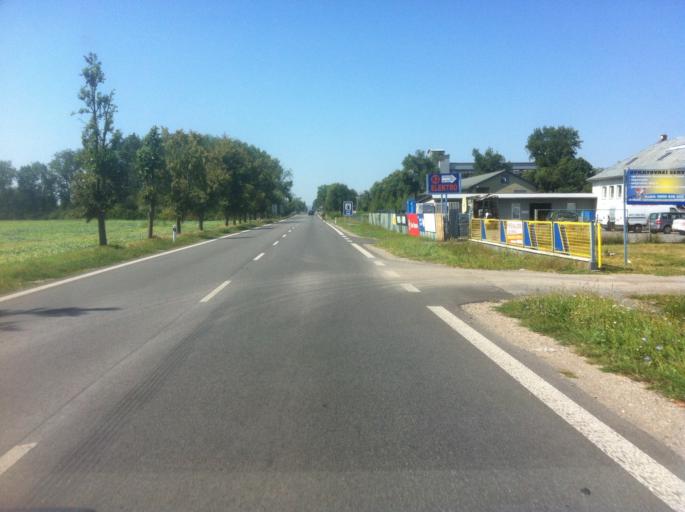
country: SK
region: Kosicky
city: Sobrance
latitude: 48.7487
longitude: 22.1703
